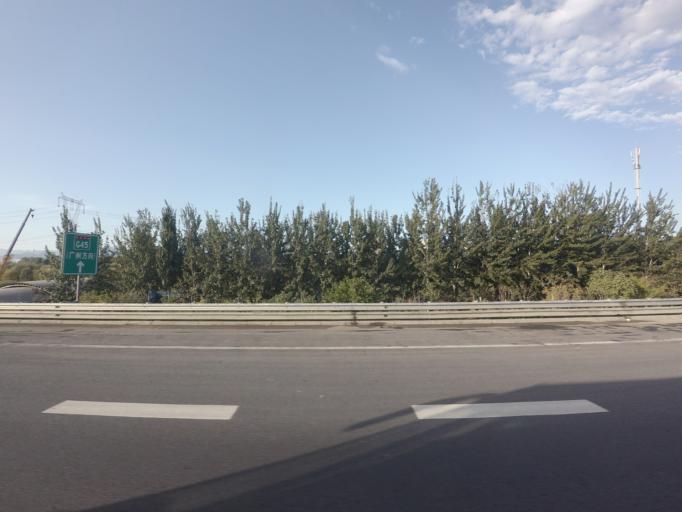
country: CN
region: Beijing
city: Yangsong
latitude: 40.2689
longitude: 116.6668
